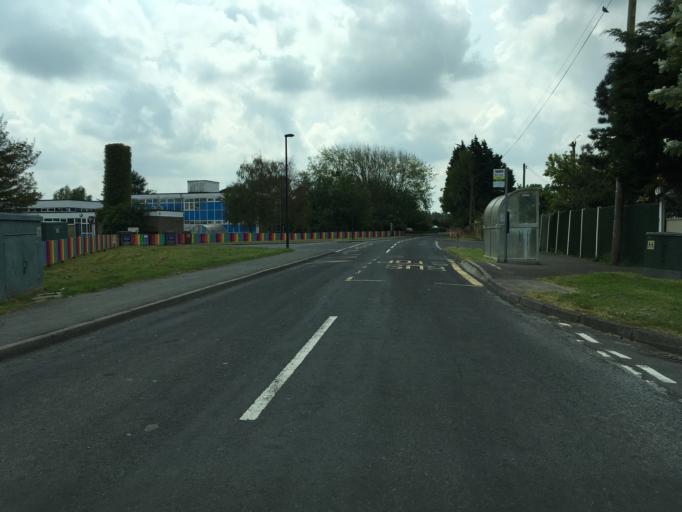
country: GB
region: England
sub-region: South Gloucestershire
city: Severn Beach
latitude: 51.5593
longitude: -2.6620
